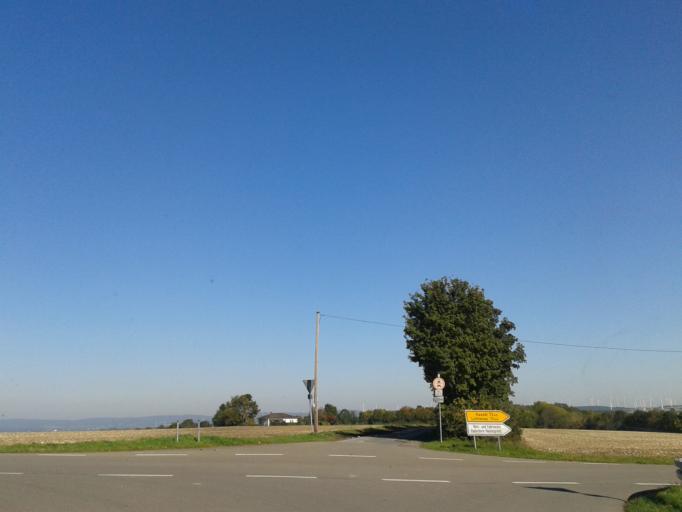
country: DE
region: North Rhine-Westphalia
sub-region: Regierungsbezirk Detmold
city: Paderborn
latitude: 51.6923
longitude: 8.7900
